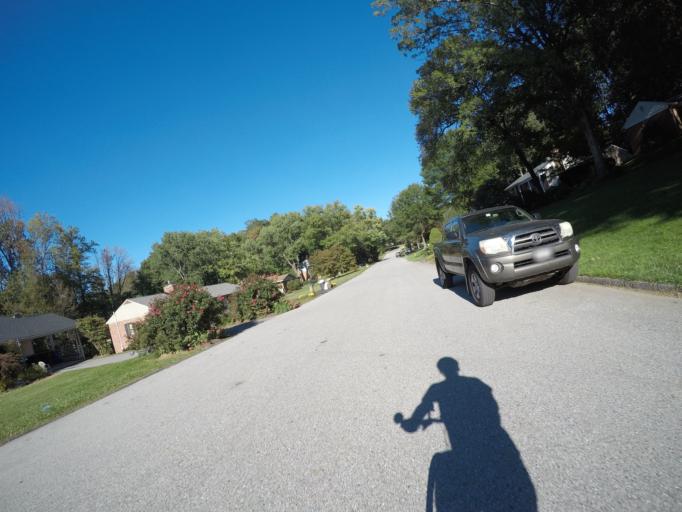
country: US
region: Maryland
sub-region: Howard County
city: Ellicott City
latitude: 39.2906
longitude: -76.8040
